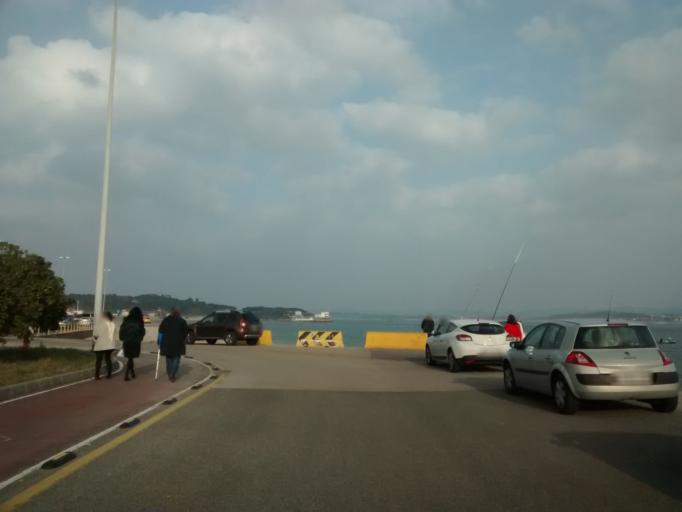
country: ES
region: Cantabria
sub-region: Provincia de Cantabria
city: Santander
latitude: 43.4633
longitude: -3.7827
